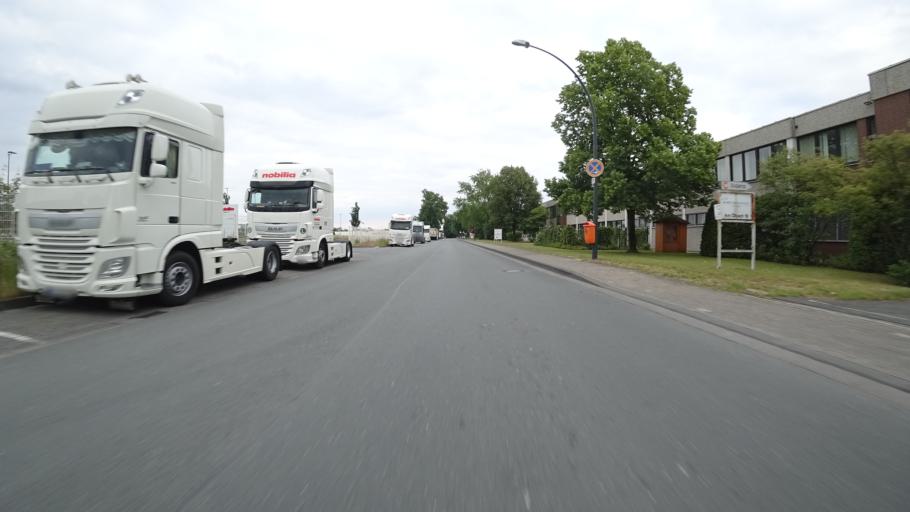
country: DE
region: North Rhine-Westphalia
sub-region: Regierungsbezirk Detmold
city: Verl
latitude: 51.8836
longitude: 8.4503
